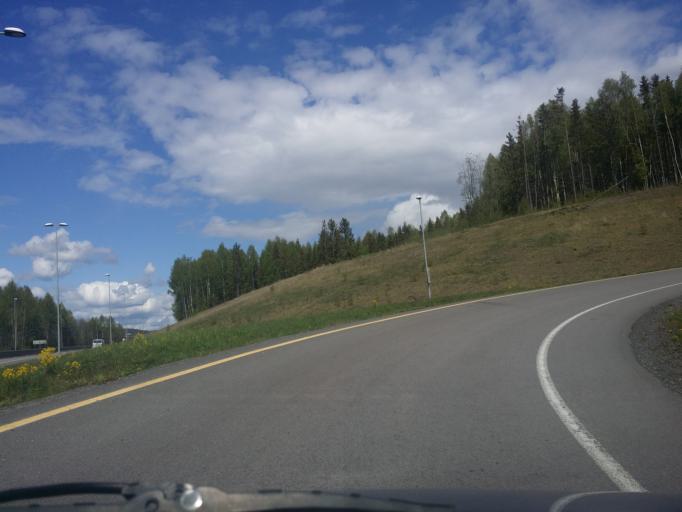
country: NO
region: Buskerud
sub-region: Ringerike
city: Honefoss
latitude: 60.1527
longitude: 10.2192
